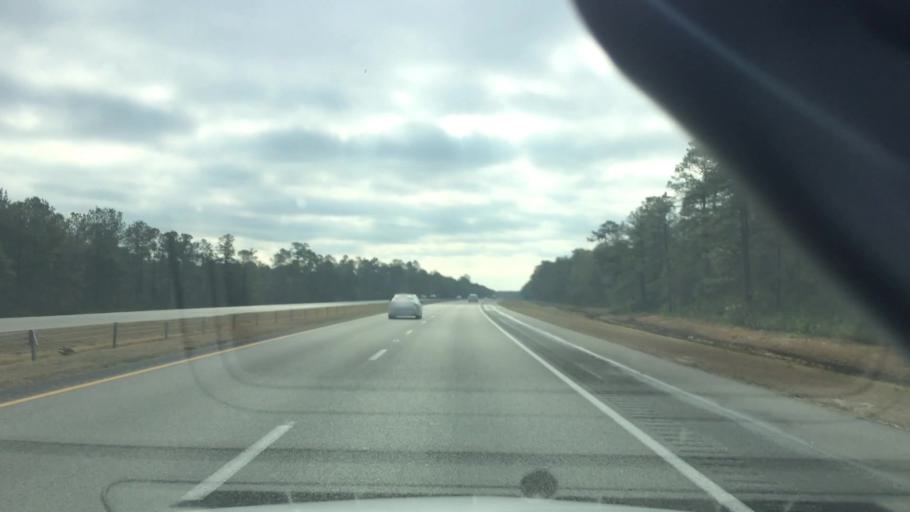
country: US
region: North Carolina
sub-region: New Hanover County
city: Castle Hayne
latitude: 34.3889
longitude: -77.8764
